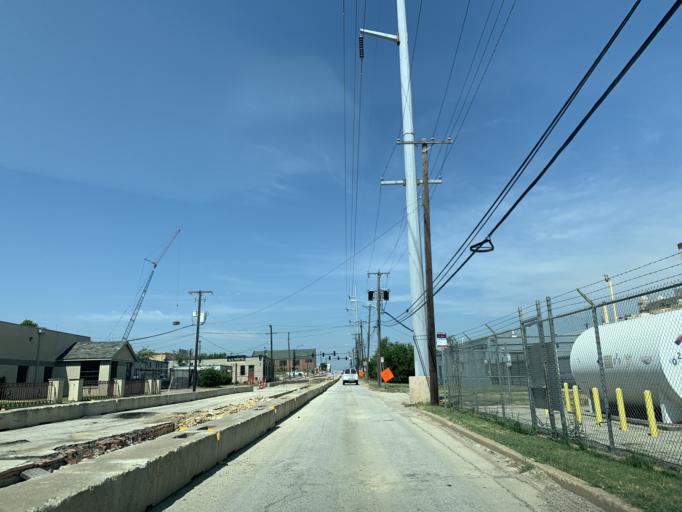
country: US
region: Texas
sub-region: Tarrant County
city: Fort Worth
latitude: 32.7436
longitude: -97.3239
